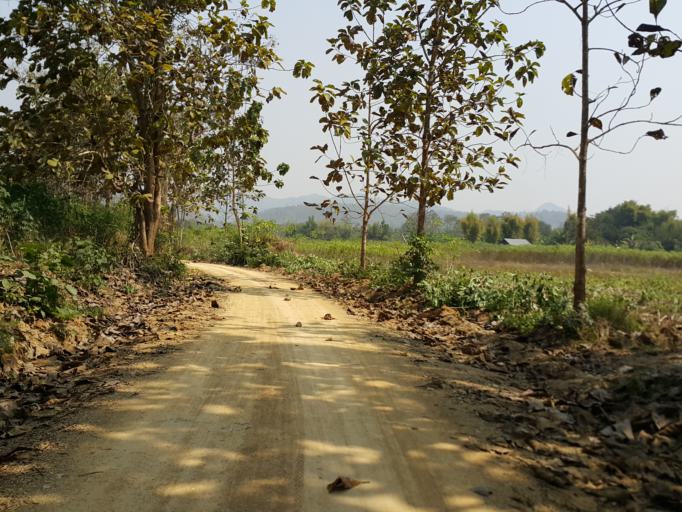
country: TH
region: Sukhothai
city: Thung Saliam
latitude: 17.3361
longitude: 99.4607
